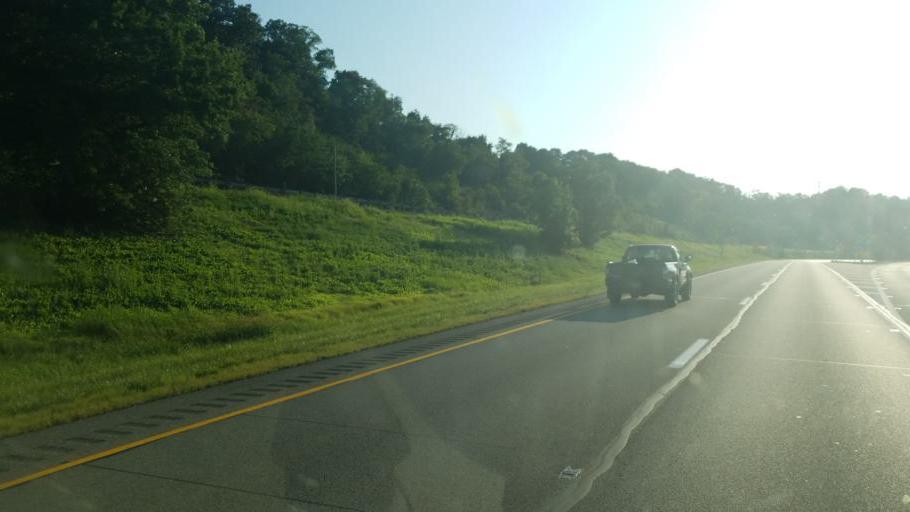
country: US
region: Pennsylvania
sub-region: Allegheny County
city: Emsworth
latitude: 40.5018
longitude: -80.1314
